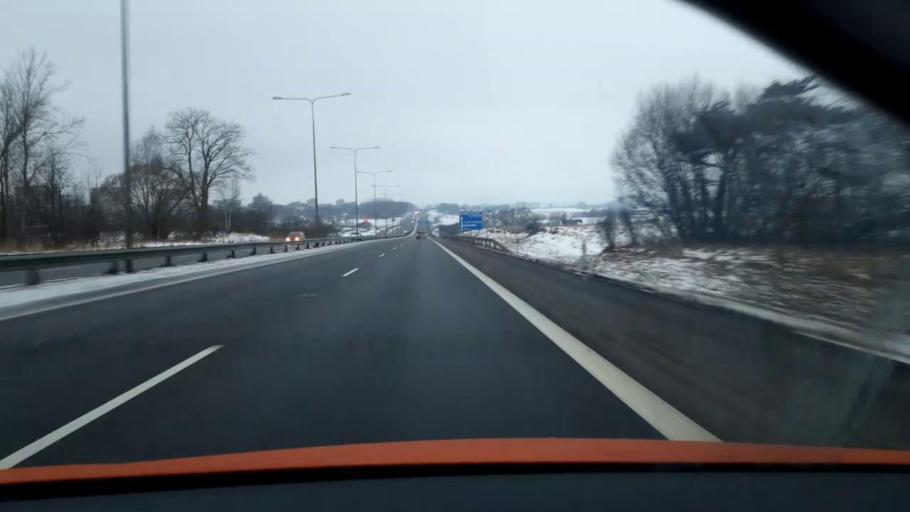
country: LT
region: Vilnius County
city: Elektrenai
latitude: 54.7893
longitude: 24.6854
